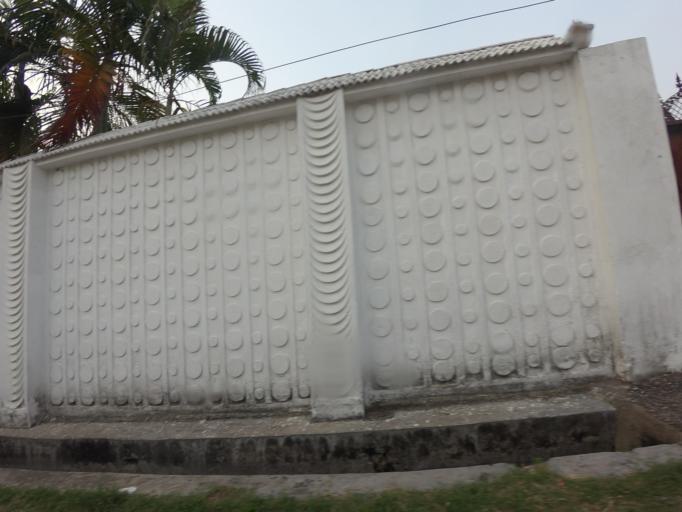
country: NP
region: Western Region
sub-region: Lumbini Zone
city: Bhairahawa
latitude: 27.5171
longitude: 83.4548
